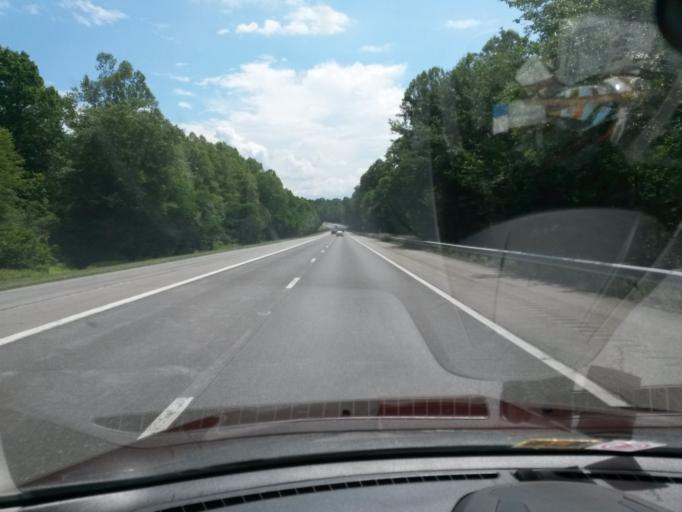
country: US
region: North Carolina
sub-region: Surry County
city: Dobson
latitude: 36.4920
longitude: -80.7454
